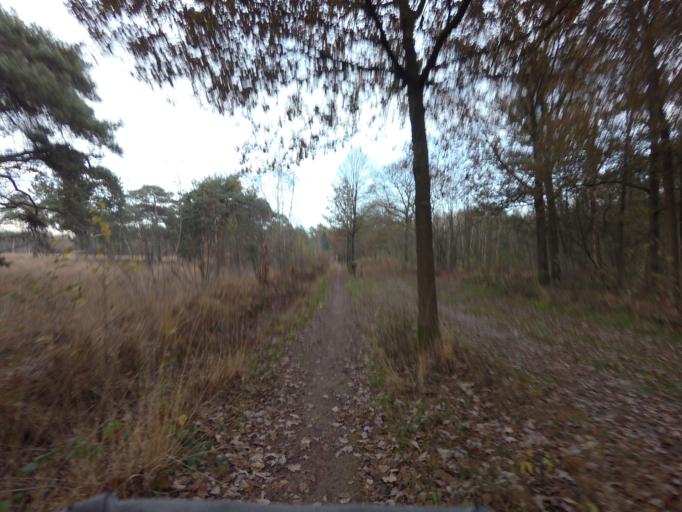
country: NL
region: North Brabant
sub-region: Gemeente Breda
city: Breda
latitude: 51.5088
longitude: 4.8100
